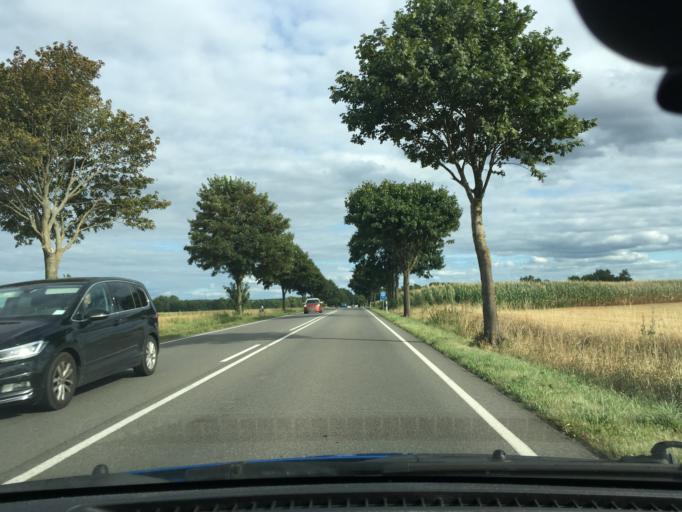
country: DE
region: Lower Saxony
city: Neu Wulmstorf
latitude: 53.4351
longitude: 9.7723
